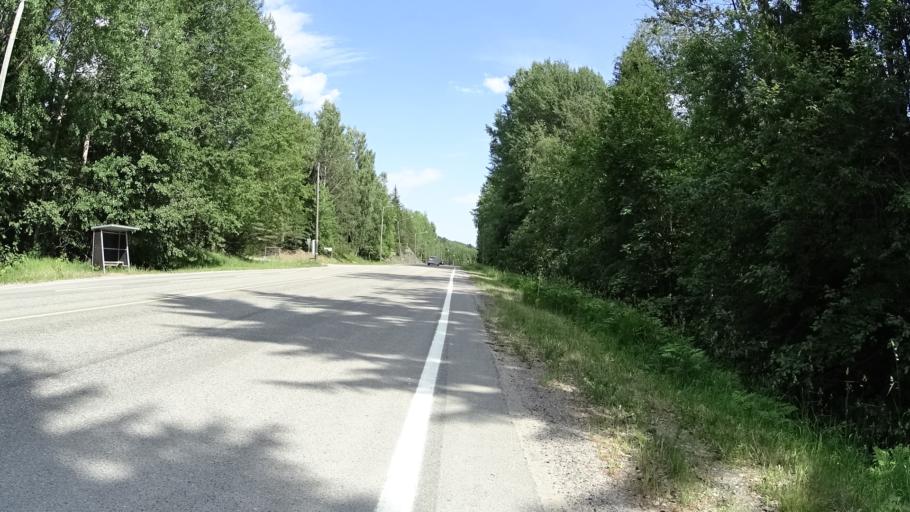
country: FI
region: Uusimaa
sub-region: Raaseporin
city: Pohja
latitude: 60.0977
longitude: 23.5951
